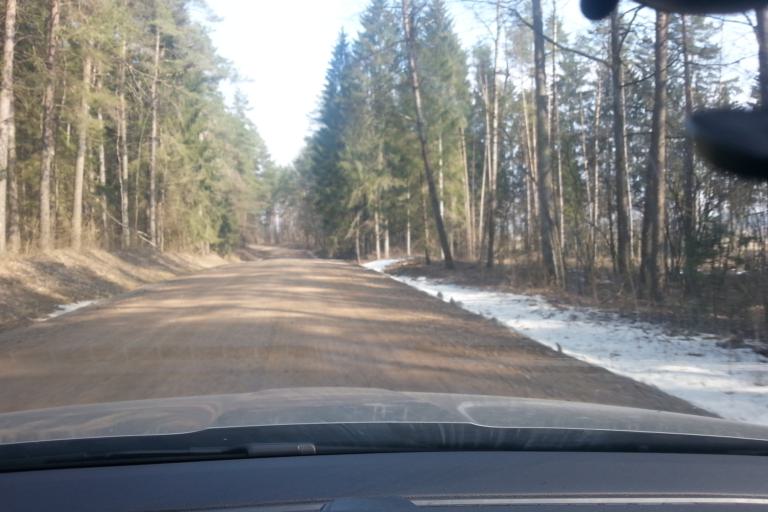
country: LT
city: Trakai
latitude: 54.5779
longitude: 24.9711
